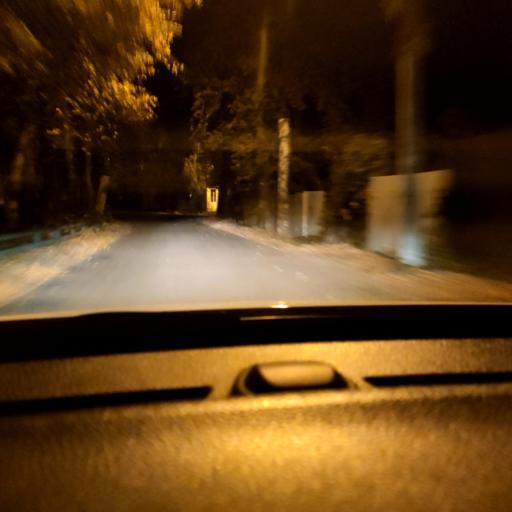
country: RU
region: Voronezj
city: Voronezh
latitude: 51.7235
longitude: 39.2240
